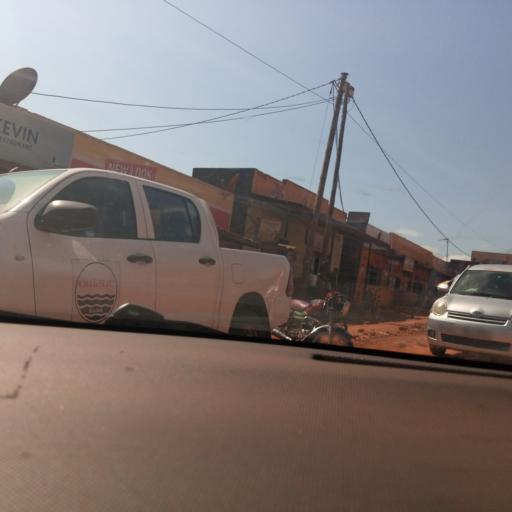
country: UG
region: Central Region
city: Masaka
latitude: -0.3161
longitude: 31.7603
